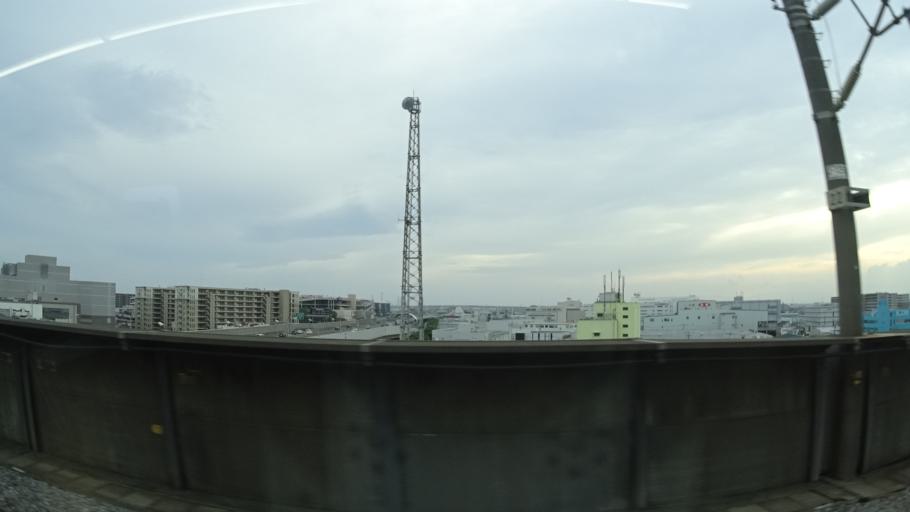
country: JP
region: Saitama
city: Shimotoda
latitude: 35.8308
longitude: 139.6560
